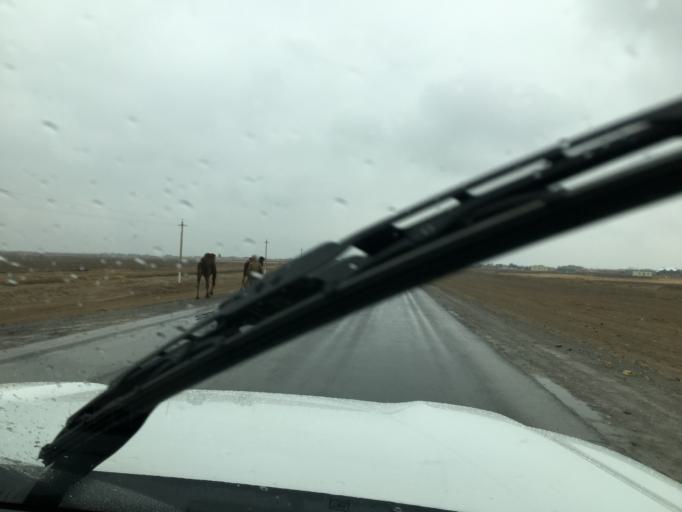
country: TM
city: Murgab
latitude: 37.4644
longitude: 62.0427
